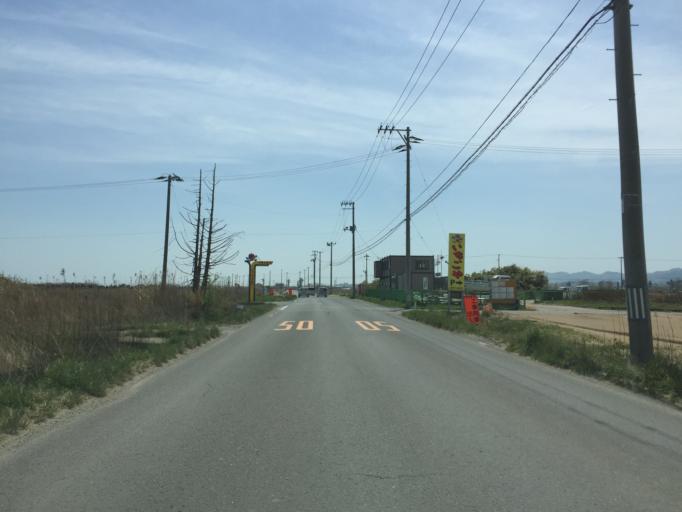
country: JP
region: Miyagi
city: Watari
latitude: 37.9840
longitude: 140.9013
